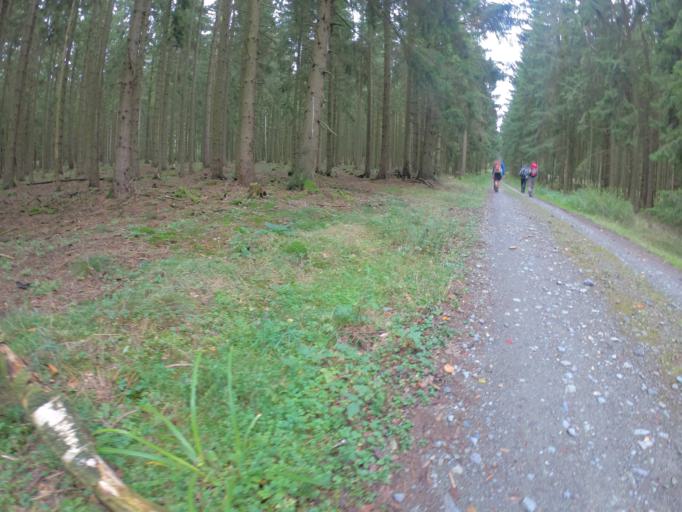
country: DE
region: Hesse
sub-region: Regierungsbezirk Darmstadt
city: Niedernhausen
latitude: 50.1883
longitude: 8.3219
